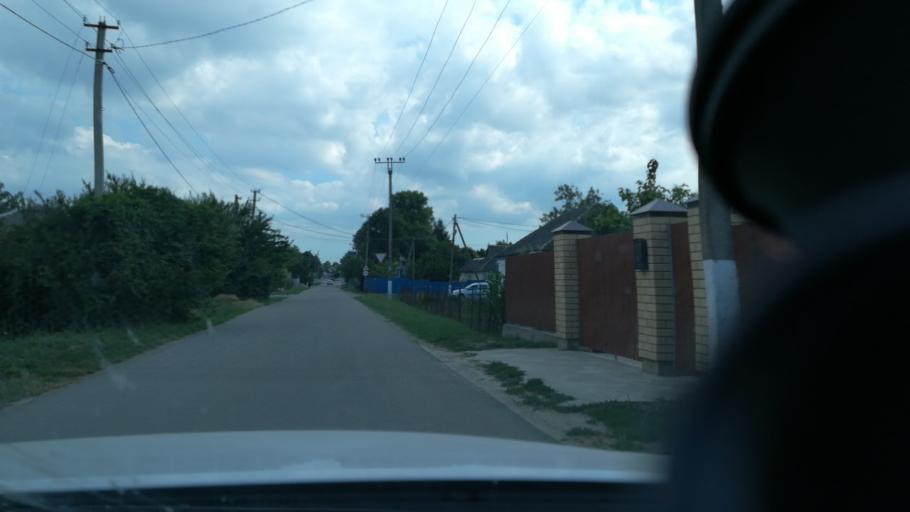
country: RU
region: Krasnodarskiy
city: Yurovka
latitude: 45.1178
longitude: 37.4152
